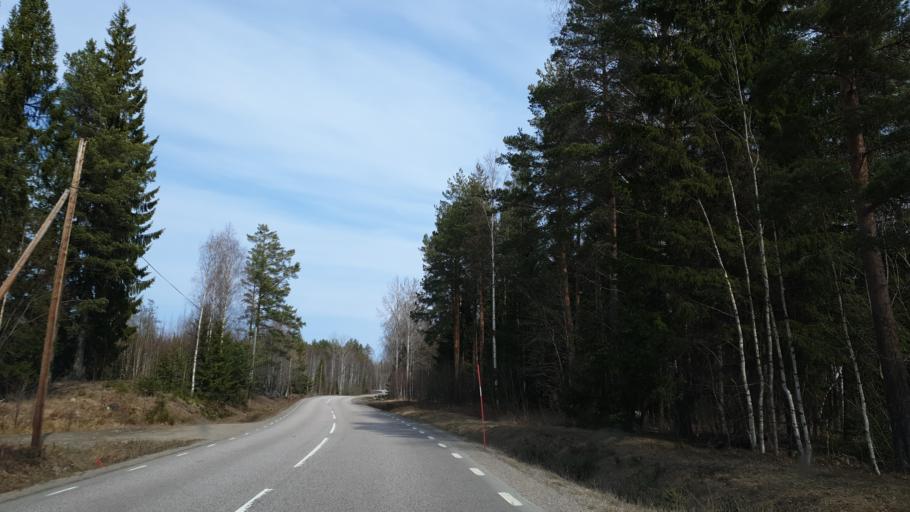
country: SE
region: Gaevleborg
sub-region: Gavle Kommun
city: Norrsundet
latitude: 60.9623
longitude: 17.0422
